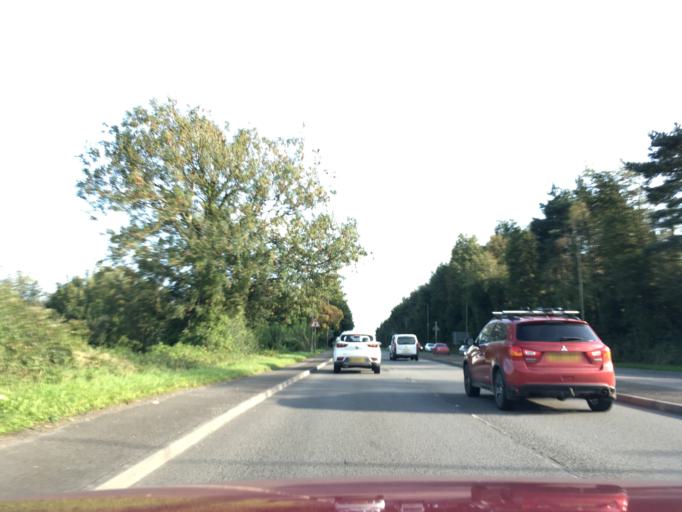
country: GB
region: Wales
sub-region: Rhondda Cynon Taf
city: Llantrisant
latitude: 51.5232
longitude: -3.3627
